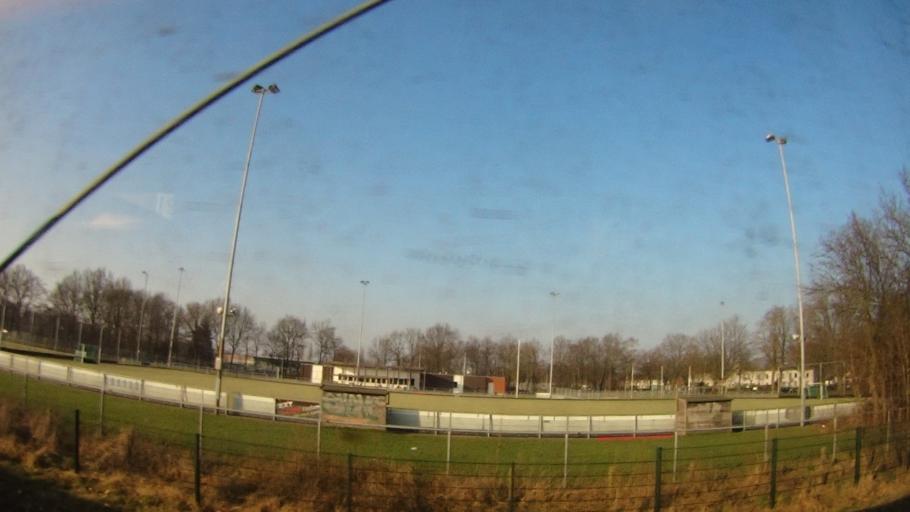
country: NL
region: Gelderland
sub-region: Gemeente Harderwijk
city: Harderwijk
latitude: 52.3394
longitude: 5.6302
